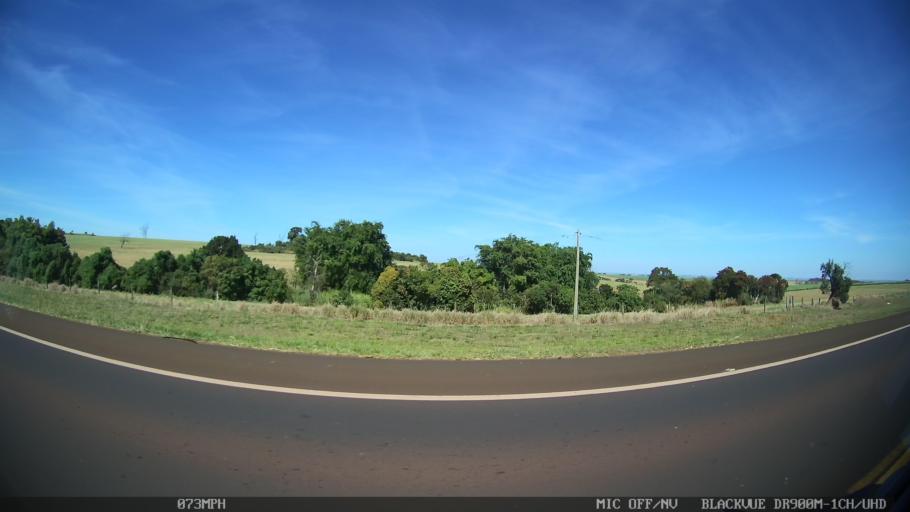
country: BR
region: Sao Paulo
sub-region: Franca
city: Franca
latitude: -20.5560
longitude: -47.5876
